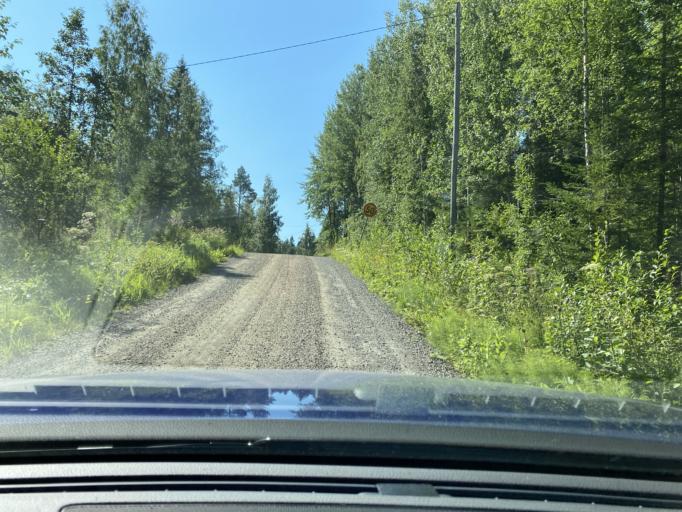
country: FI
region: Central Finland
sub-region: Jaemsae
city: Jaemsae
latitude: 61.8594
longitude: 25.3942
